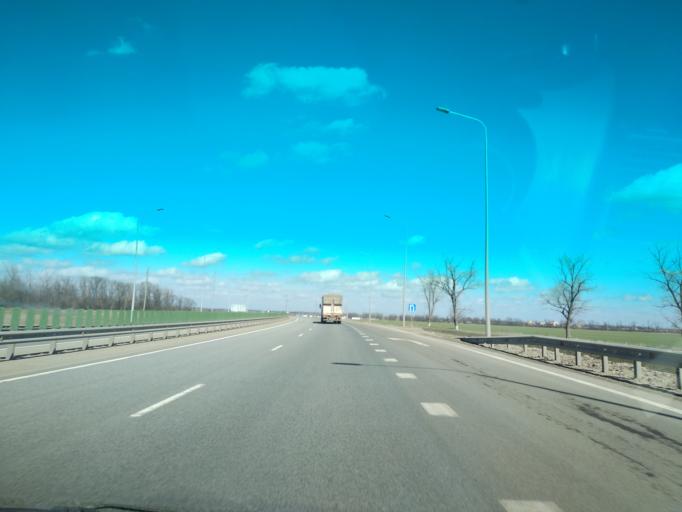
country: RU
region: Krasnodarskiy
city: Platnirovskaya
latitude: 45.4592
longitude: 39.3878
